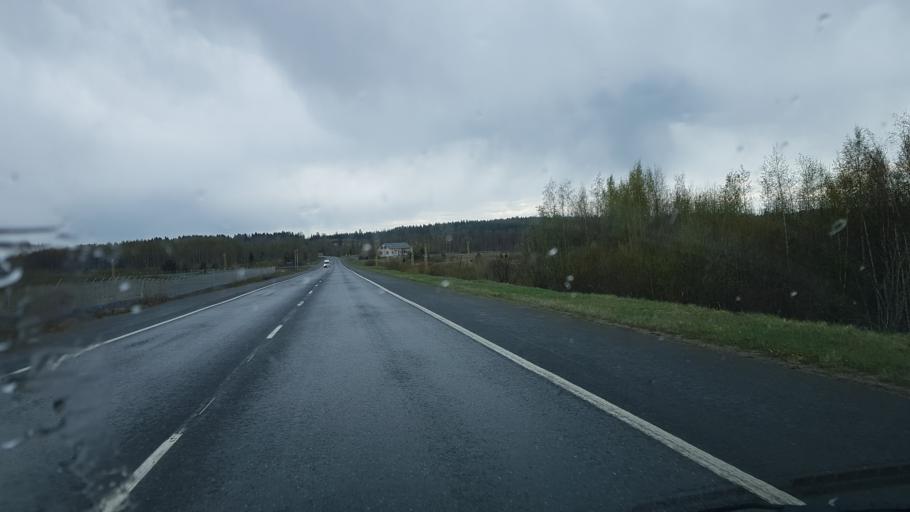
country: FI
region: Pirkanmaa
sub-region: Tampere
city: Pirkkala
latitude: 61.4187
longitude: 23.6344
